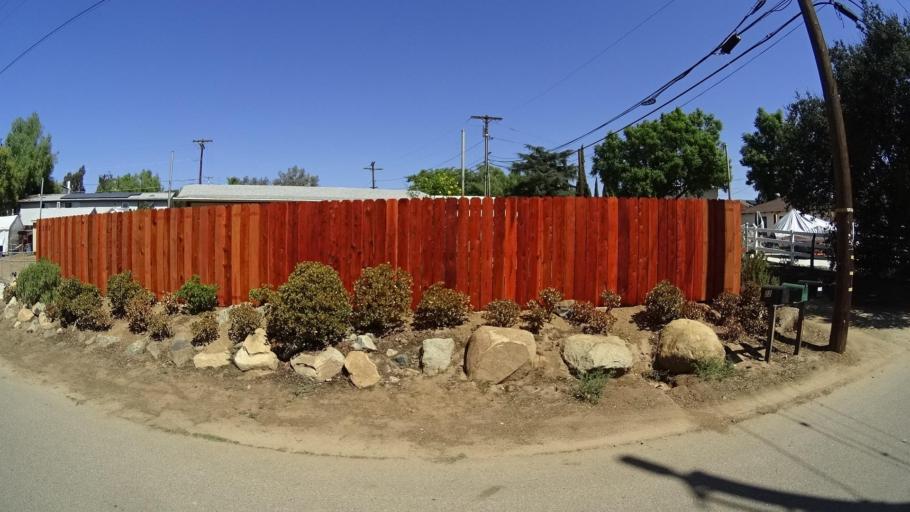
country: US
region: California
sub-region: San Diego County
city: Crest
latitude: 32.8000
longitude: -116.8644
